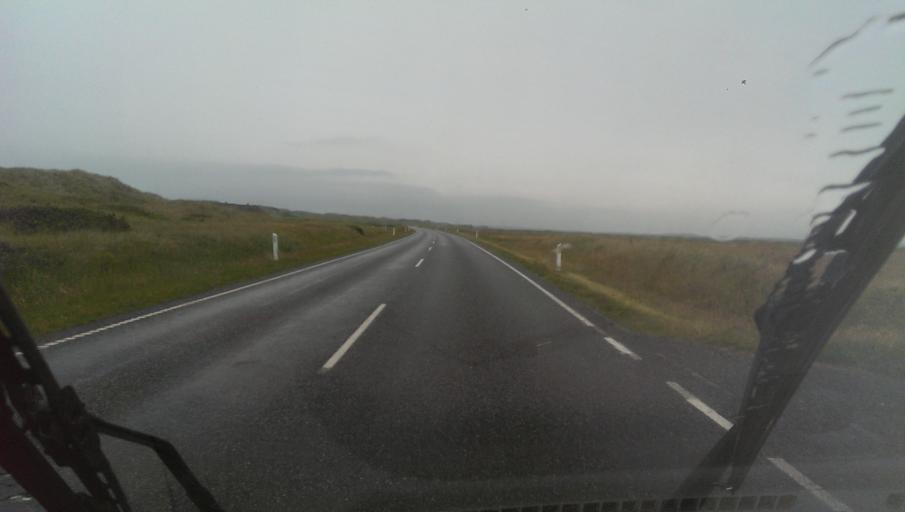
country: DK
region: Central Jutland
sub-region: Ringkobing-Skjern Kommune
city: Ringkobing
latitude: 56.1995
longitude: 8.1311
